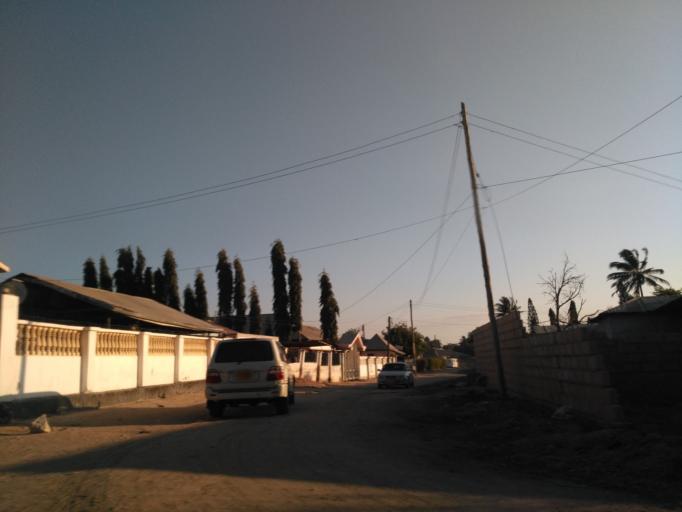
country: TZ
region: Dodoma
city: Dodoma
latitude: -6.1724
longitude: 35.7341
